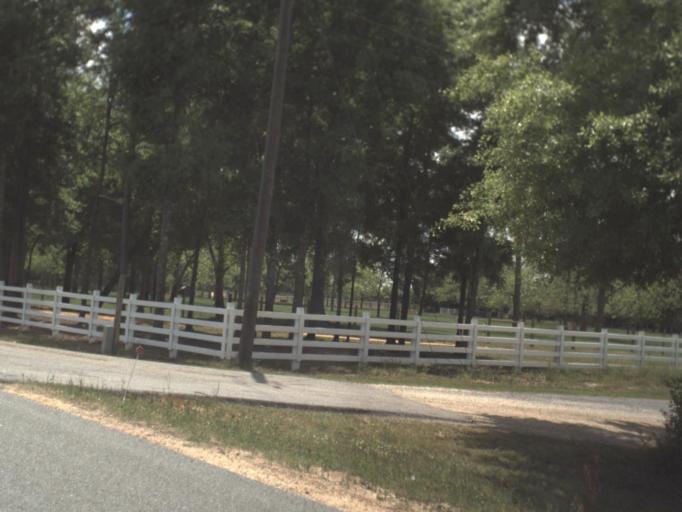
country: US
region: Alabama
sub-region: Escambia County
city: Atmore
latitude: 30.9032
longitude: -87.4813
